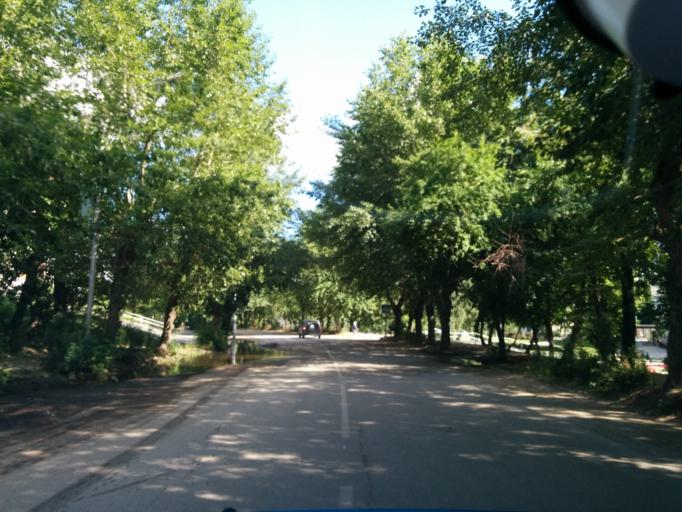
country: RU
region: Perm
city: Perm
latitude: 58.0080
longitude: 56.1955
